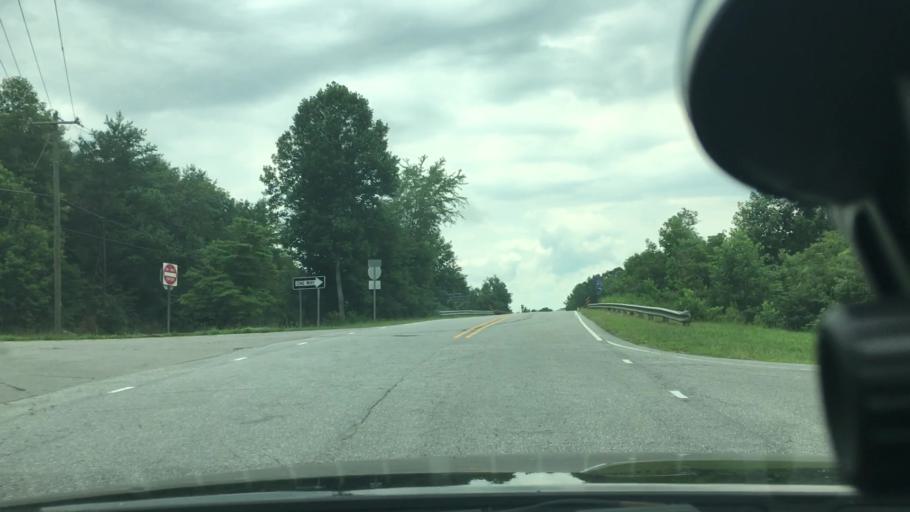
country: US
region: North Carolina
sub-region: McDowell County
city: West Marion
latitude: 35.6346
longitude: -82.0025
